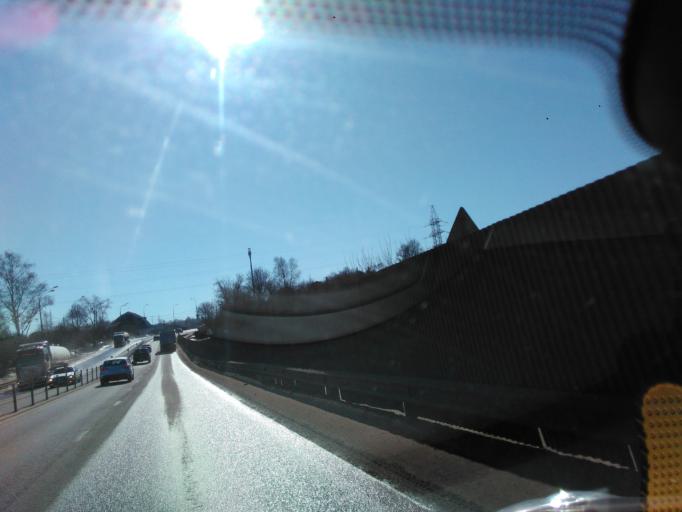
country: RU
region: Moskovskaya
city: Iksha
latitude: 56.1639
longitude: 37.5010
